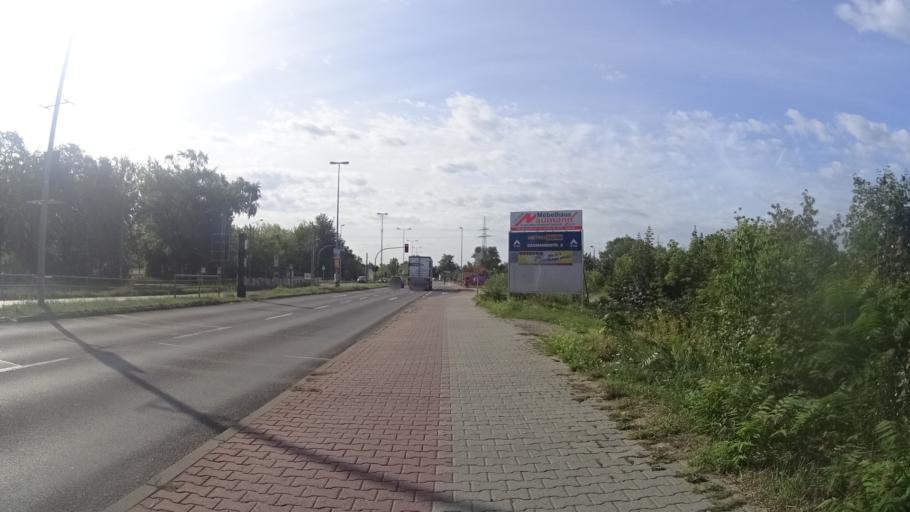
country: DE
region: Brandenburg
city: Brandenburg an der Havel
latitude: 52.4229
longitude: 12.5316
